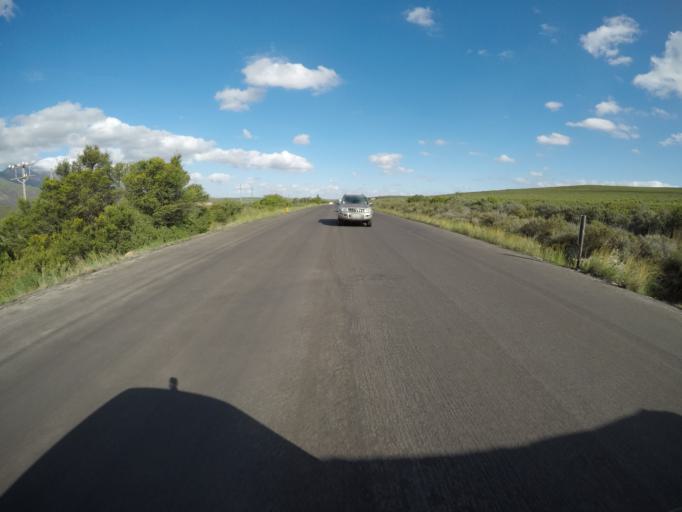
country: ZA
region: Western Cape
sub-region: Cape Winelands District Municipality
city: Ashton
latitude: -33.9338
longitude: 20.2107
